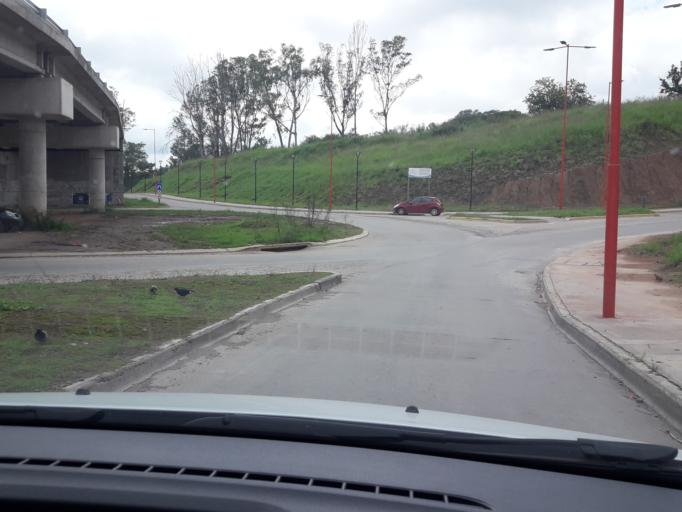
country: AR
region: Jujuy
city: San Salvador de Jujuy
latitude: -24.1794
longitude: -65.3270
